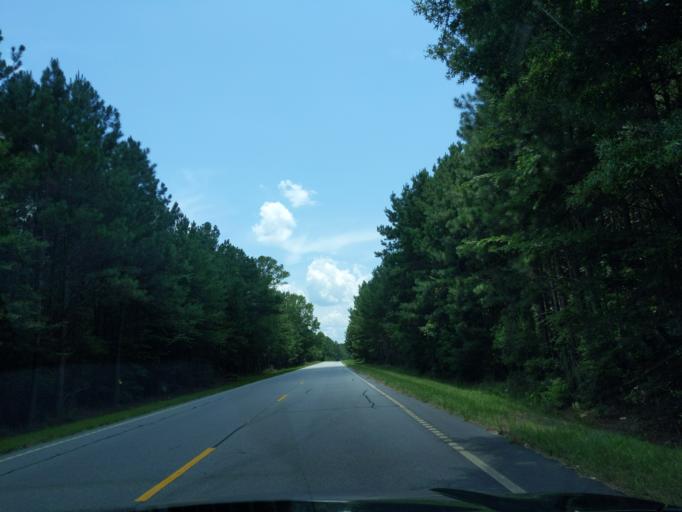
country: US
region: South Carolina
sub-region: Greenwood County
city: Ninety Six
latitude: 33.9733
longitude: -82.0457
